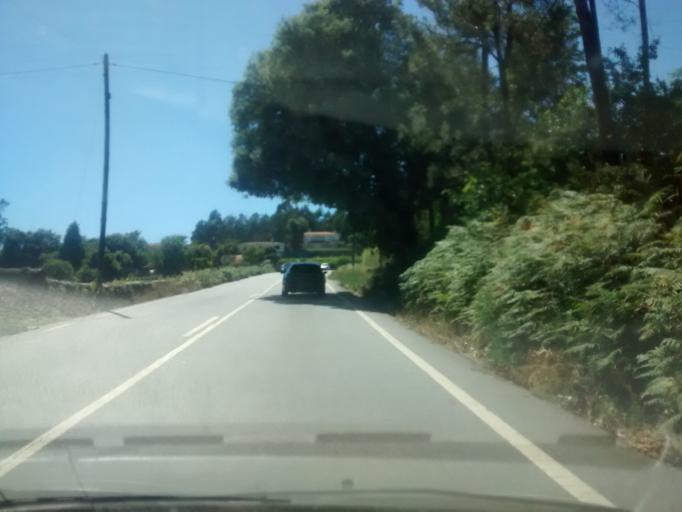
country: PT
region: Braga
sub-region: Barcelos
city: Galegos
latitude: 41.5321
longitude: -8.5522
